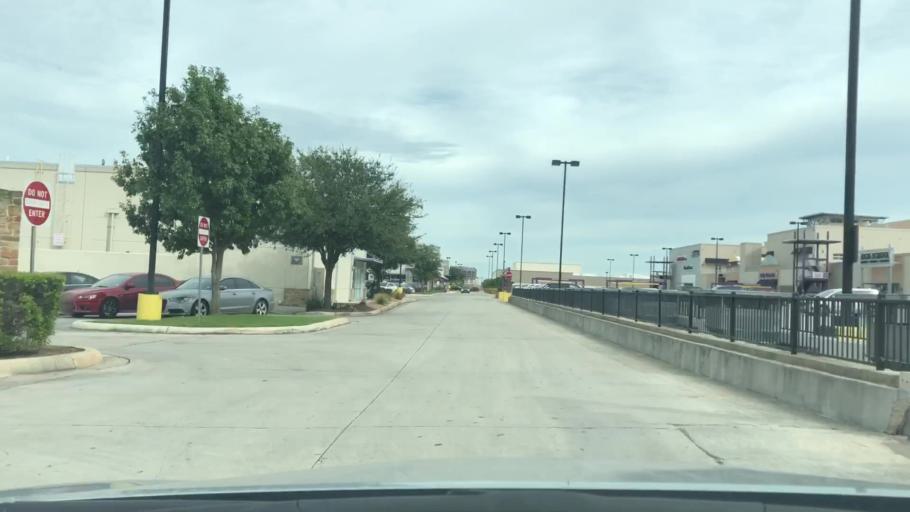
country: US
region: Texas
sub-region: Bexar County
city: Castle Hills
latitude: 29.5191
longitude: -98.5050
